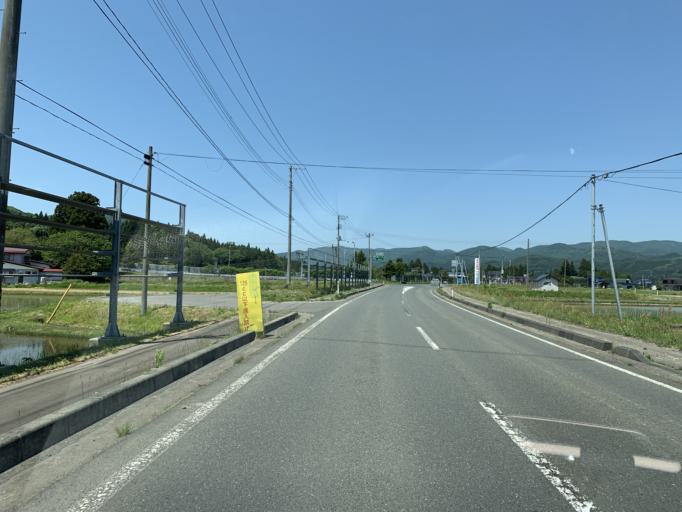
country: JP
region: Iwate
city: Kitakami
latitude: 39.2958
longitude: 140.9839
